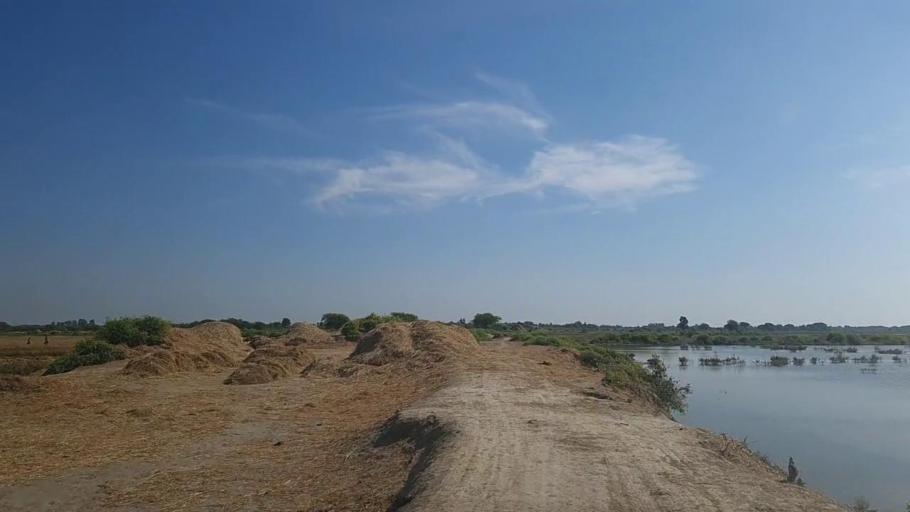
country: PK
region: Sindh
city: Mirpur Batoro
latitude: 24.7535
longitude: 68.3063
